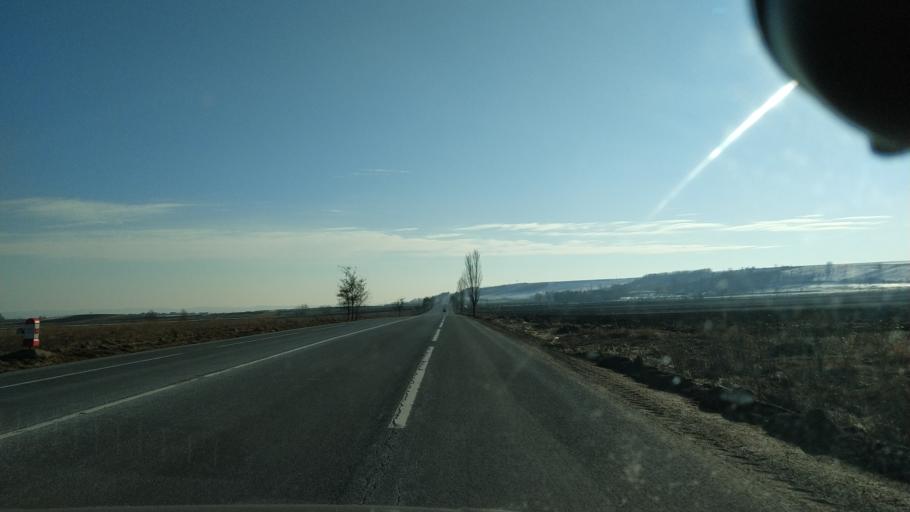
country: RO
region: Iasi
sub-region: Comuna Rachiteni
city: Izvoarele
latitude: 47.0546
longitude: 26.8769
